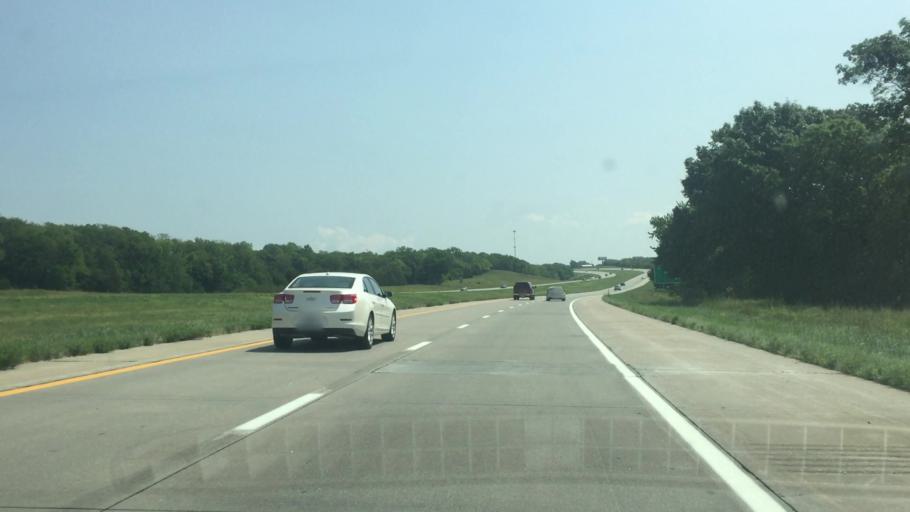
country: US
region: Kansas
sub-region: Osage County
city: Lyndon
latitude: 38.4858
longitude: -95.4879
